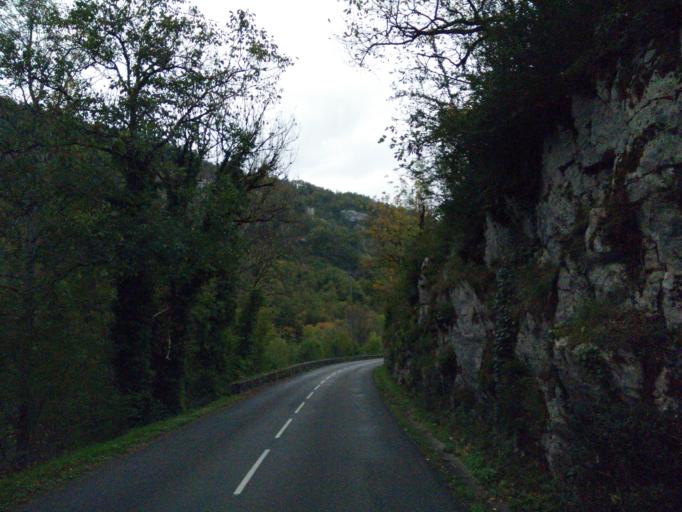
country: FR
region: Midi-Pyrenees
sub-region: Departement du Lot
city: Lalbenque
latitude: 44.4919
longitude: 1.6548
